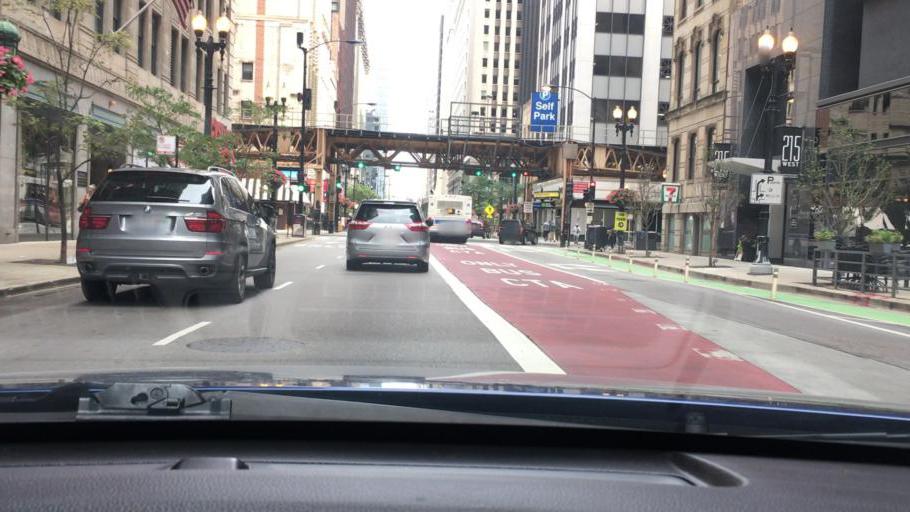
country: US
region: Illinois
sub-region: Cook County
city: Chicago
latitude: 41.8832
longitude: -87.6346
